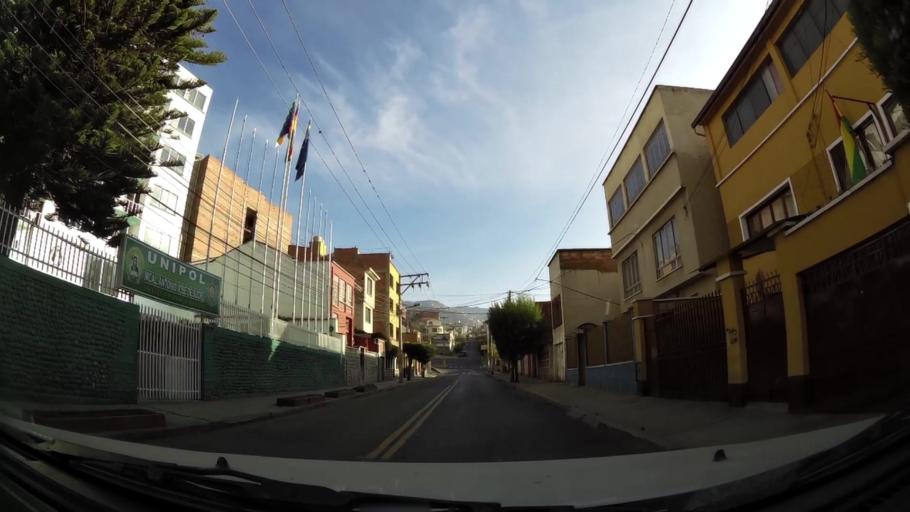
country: BO
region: La Paz
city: La Paz
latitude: -16.4918
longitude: -68.1241
